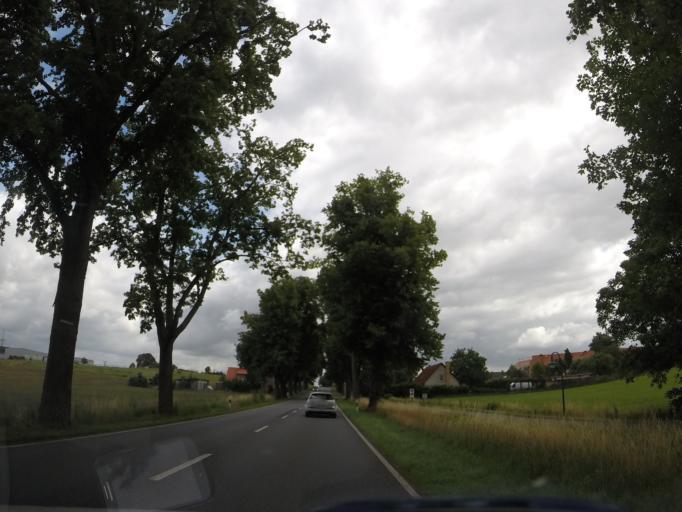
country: DE
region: Mecklenburg-Vorpommern
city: Lalendorf
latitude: 53.7656
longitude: 12.3454
